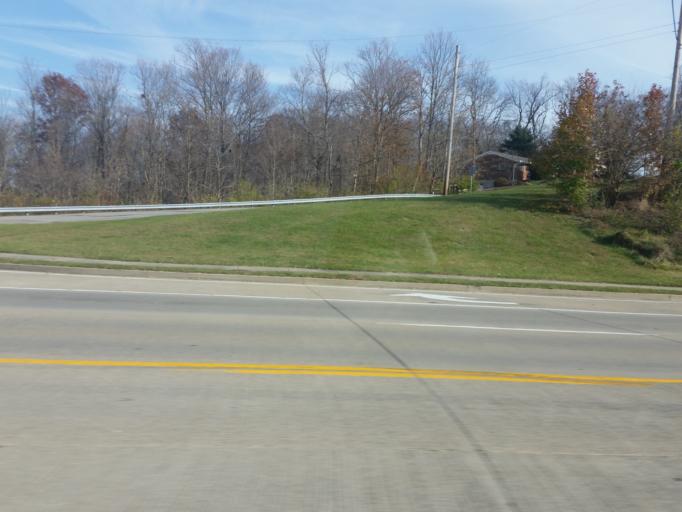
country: US
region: Kentucky
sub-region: Campbell County
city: Alexandria
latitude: 38.9519
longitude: -84.3935
